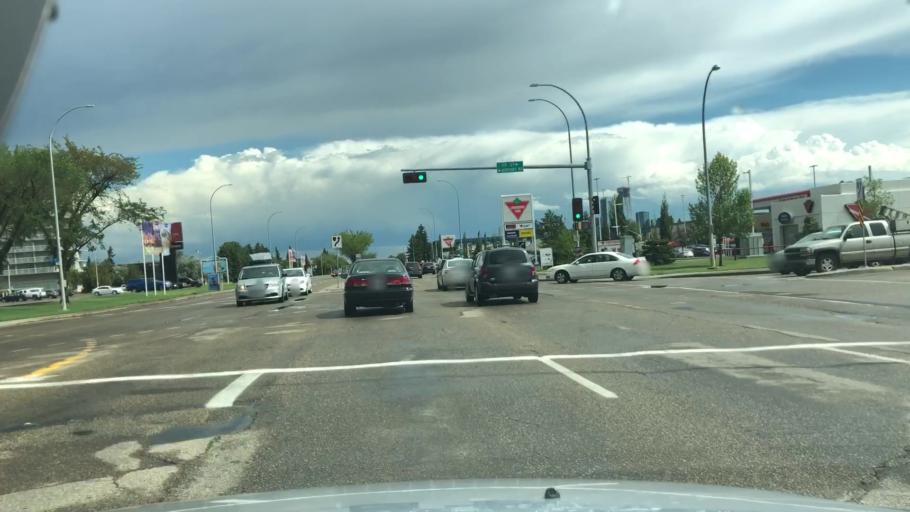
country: CA
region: Alberta
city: Edmonton
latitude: 53.5686
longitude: -113.5267
